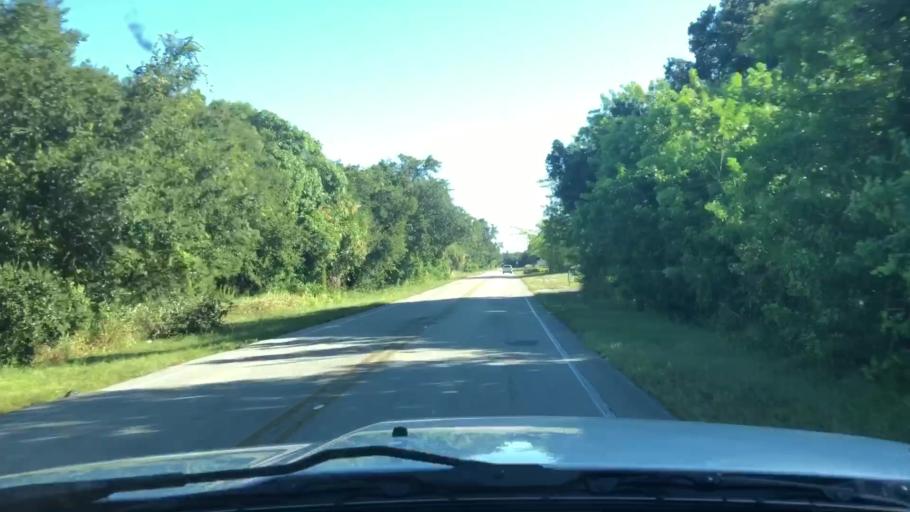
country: US
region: Florida
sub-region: Indian River County
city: Florida Ridge
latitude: 27.5723
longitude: -80.3750
